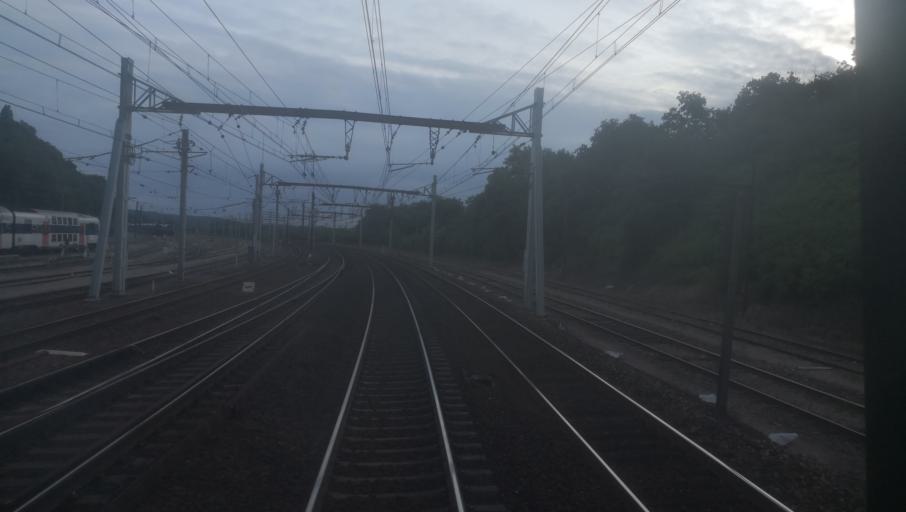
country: FR
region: Ile-de-France
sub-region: Departement de l'Essonne
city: Morigny-Champigny
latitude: 48.4409
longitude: 2.1672
